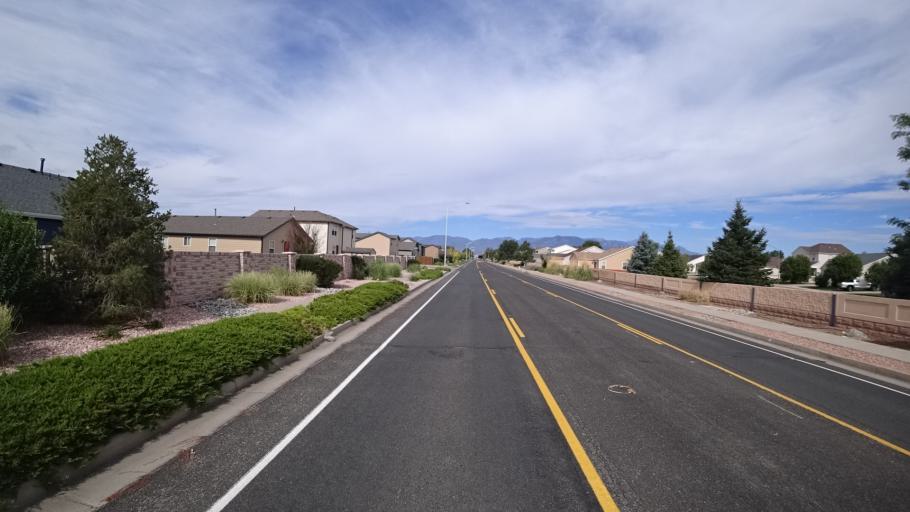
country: US
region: Colorado
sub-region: El Paso County
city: Fountain
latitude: 38.7084
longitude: -104.6911
